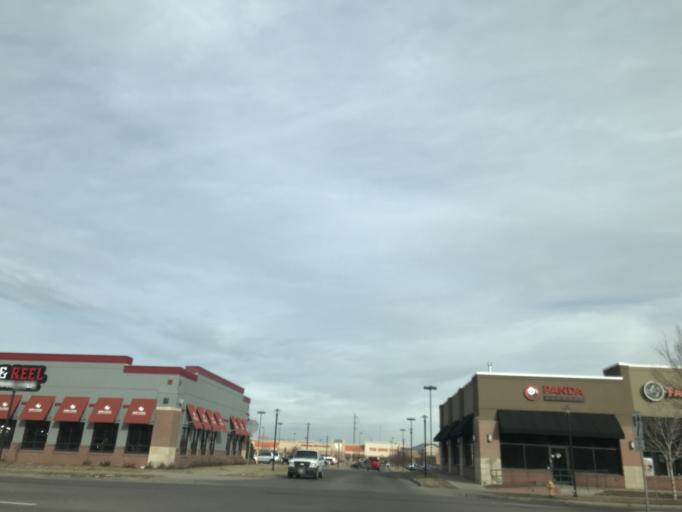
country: US
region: Colorado
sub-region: Adams County
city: Commerce City
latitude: 39.7672
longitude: -104.9008
